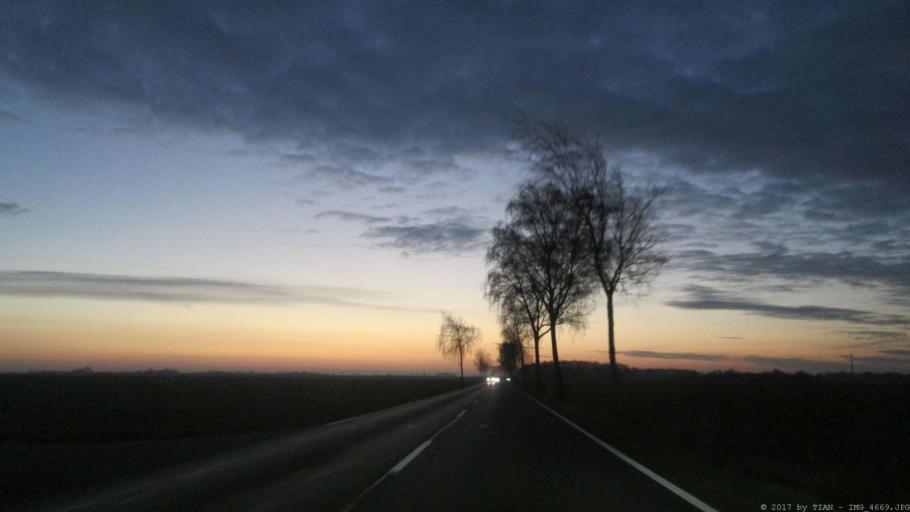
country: DE
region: Lower Saxony
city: Wittingen
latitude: 52.7501
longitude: 10.7256
